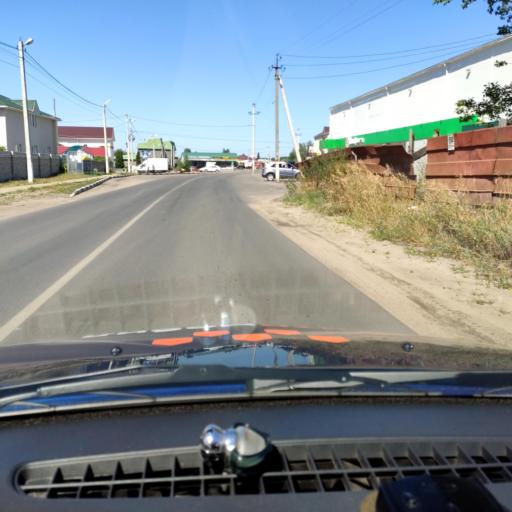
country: RU
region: Voronezj
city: Podgornoye
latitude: 51.7893
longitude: 39.1459
